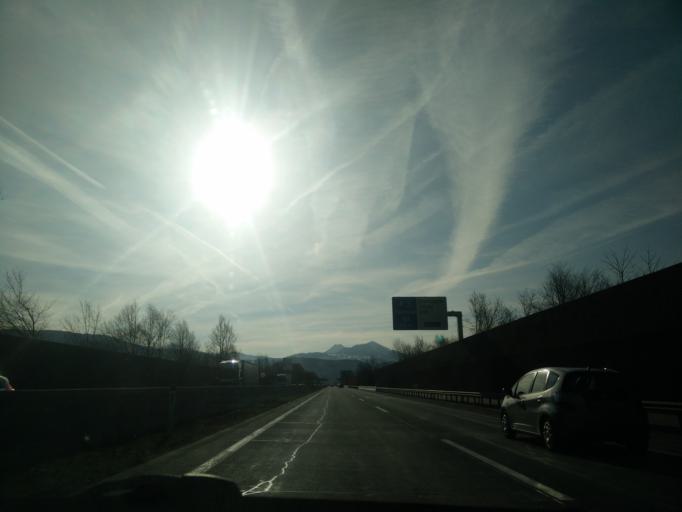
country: AT
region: Salzburg
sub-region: Politischer Bezirk Salzburg-Umgebung
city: Grodig
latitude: 47.7449
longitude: 13.0356
